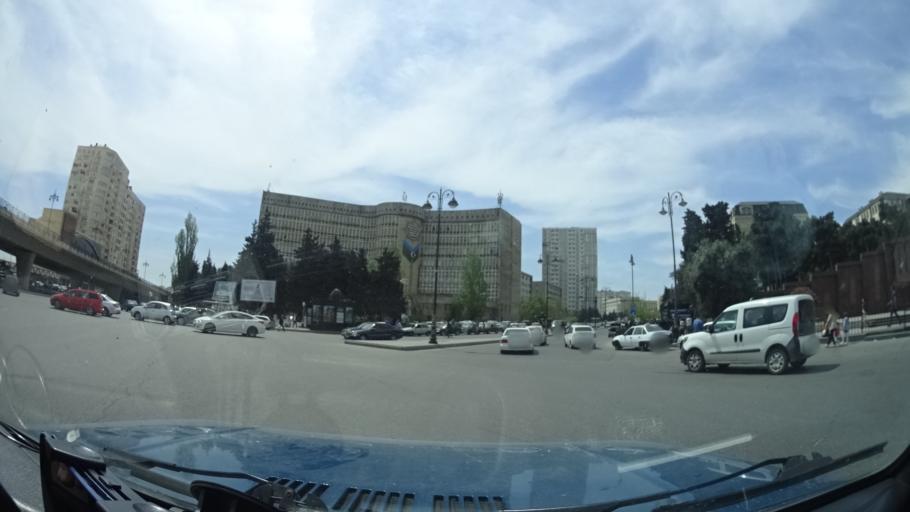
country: AZ
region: Baki
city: Khodzhi-Gasan
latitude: 40.4038
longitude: 49.8074
